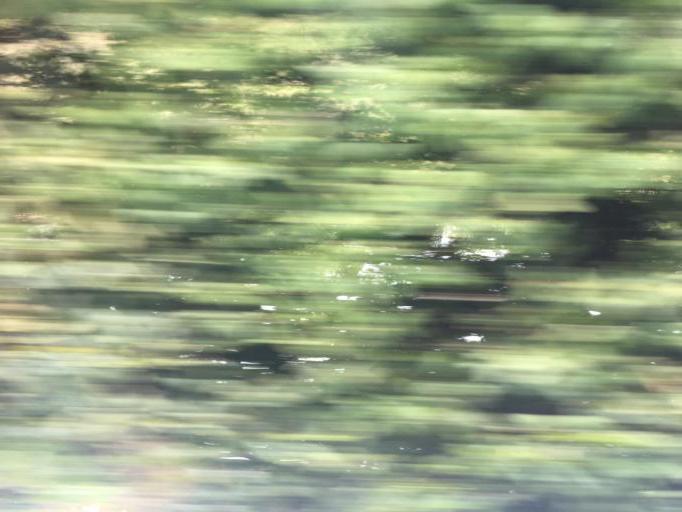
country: DE
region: Saxony
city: Coswig
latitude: 51.0822
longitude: 13.6032
